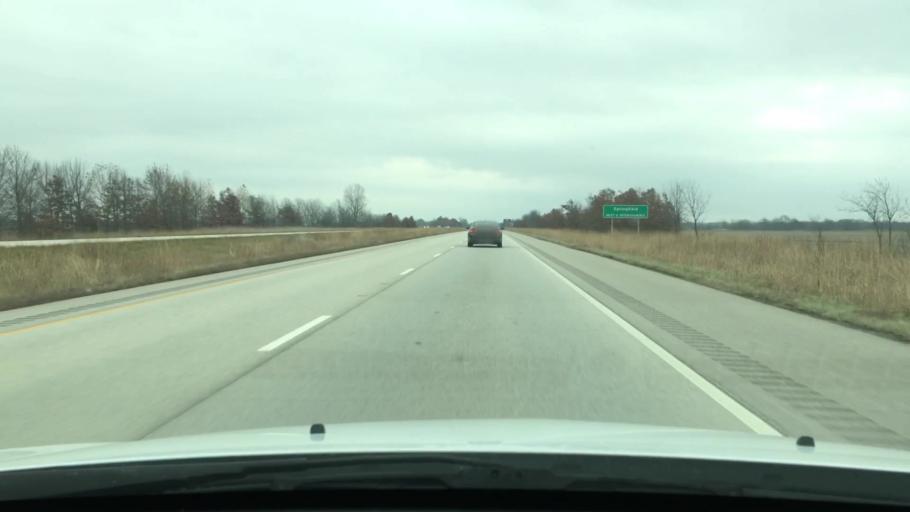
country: US
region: Illinois
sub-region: Sangamon County
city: Jerome
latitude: 39.7516
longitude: -89.7916
